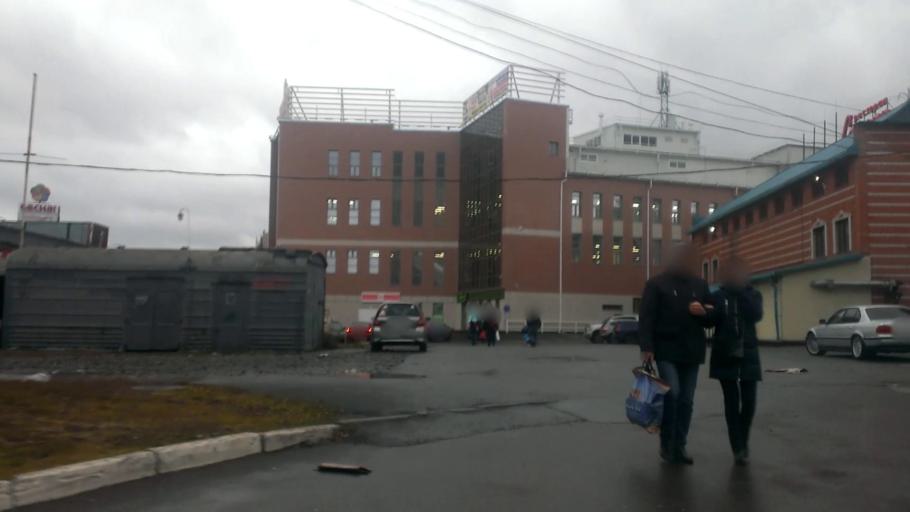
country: RU
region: Altai Krai
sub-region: Gorod Barnaulskiy
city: Barnaul
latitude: 53.3584
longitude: 83.6983
